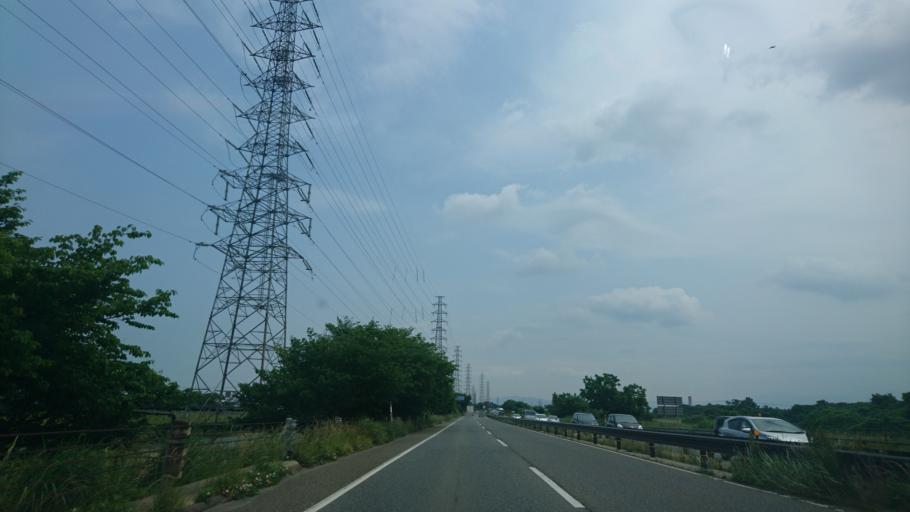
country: JP
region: Niigata
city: Suibara
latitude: 37.9480
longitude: 139.1985
